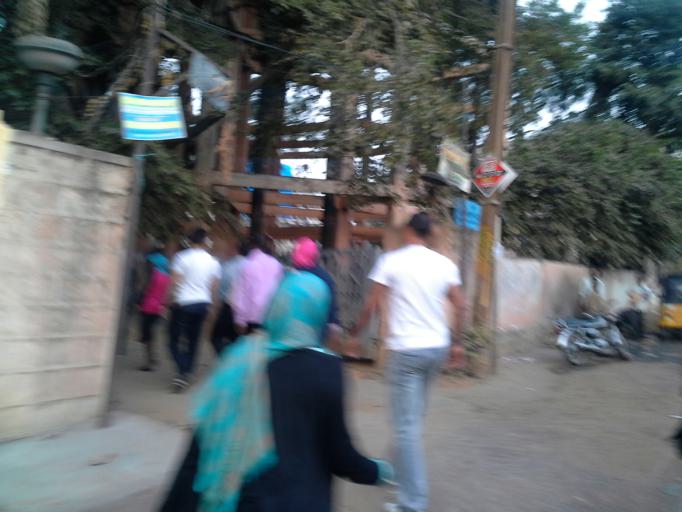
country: IN
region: Telangana
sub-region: Hyderabad
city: Malkajgiri
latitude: 17.4264
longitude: 78.5173
